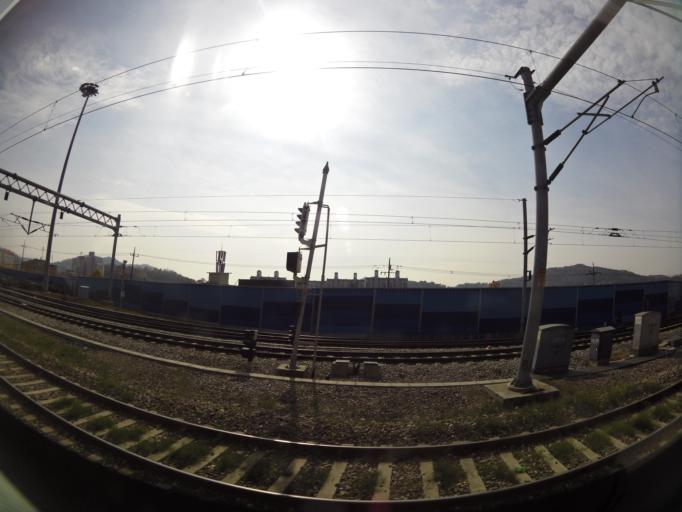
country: KR
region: Daejeon
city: Songgang-dong
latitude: 36.5332
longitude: 127.3616
